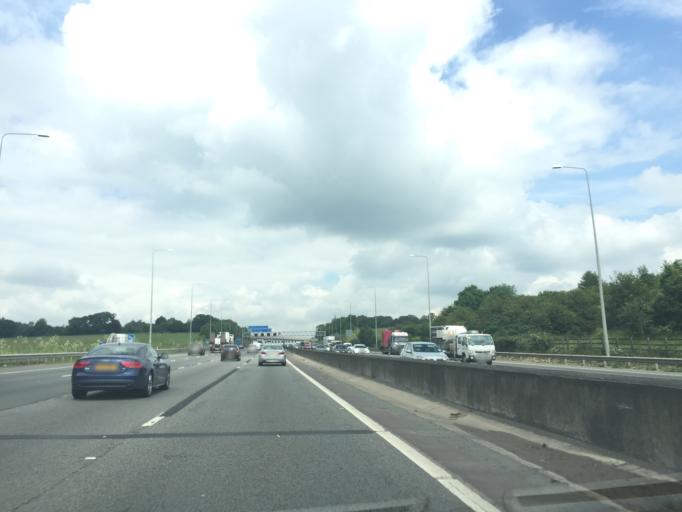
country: GB
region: England
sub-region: Buckinghamshire
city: Chalfont Saint Peter
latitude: 51.6294
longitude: -0.5198
